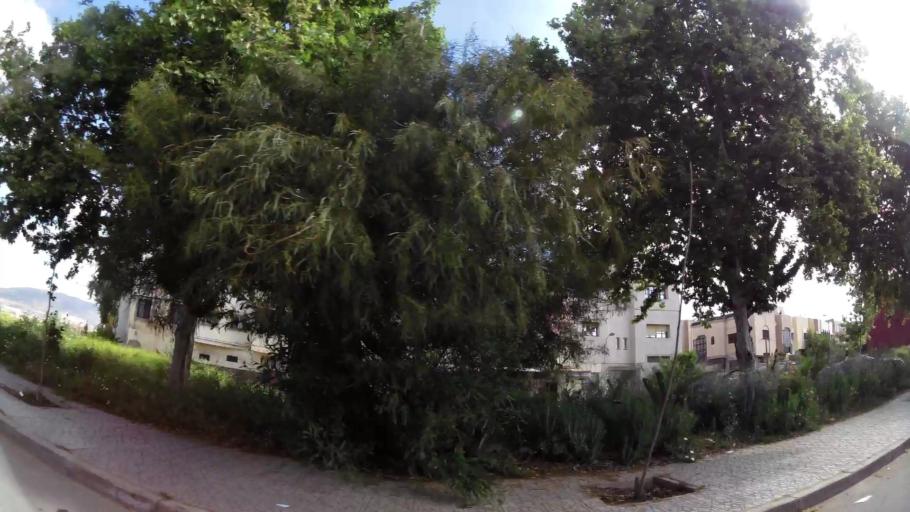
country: MA
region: Fes-Boulemane
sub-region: Fes
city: Fes
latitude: 34.0264
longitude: -5.0245
